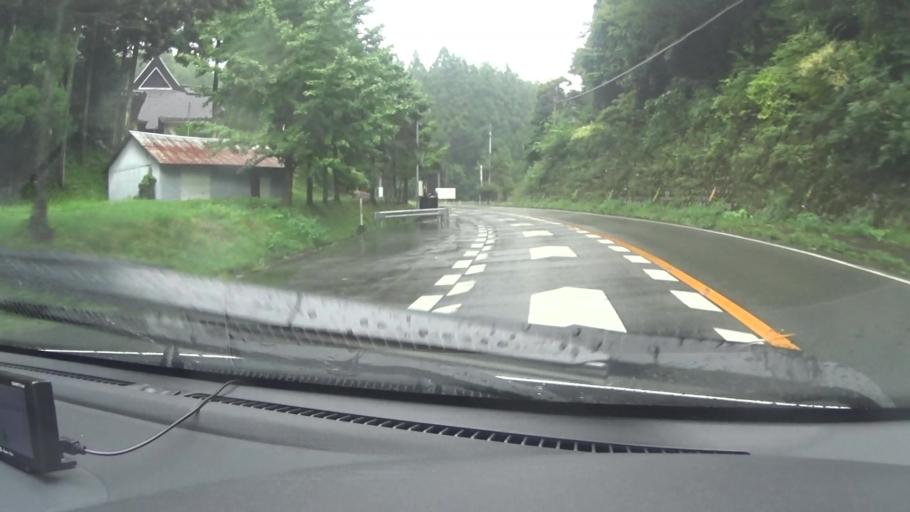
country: JP
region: Kyoto
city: Ayabe
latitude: 35.2223
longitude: 135.3380
